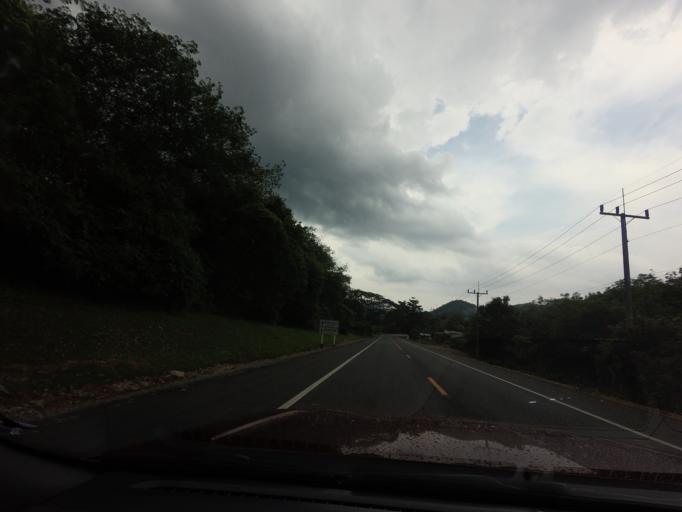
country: TH
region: Yala
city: Ban Nang Sata
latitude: 6.2288
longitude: 101.2202
